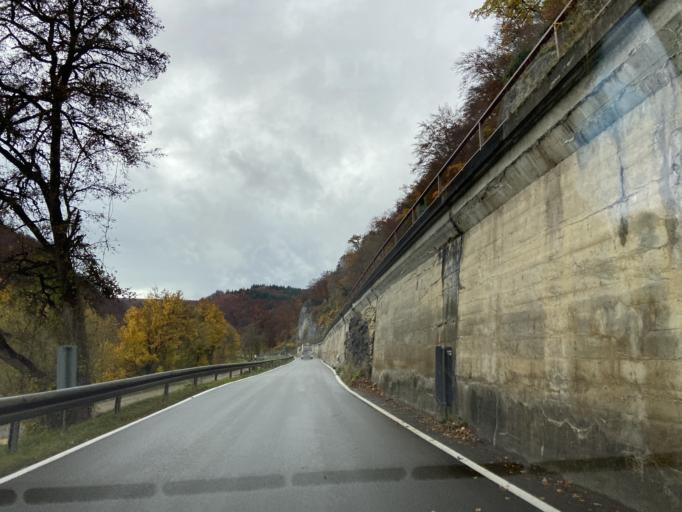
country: DE
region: Baden-Wuerttemberg
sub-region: Tuebingen Region
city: Stetten am Kalten Markt
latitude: 48.0841
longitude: 9.0931
